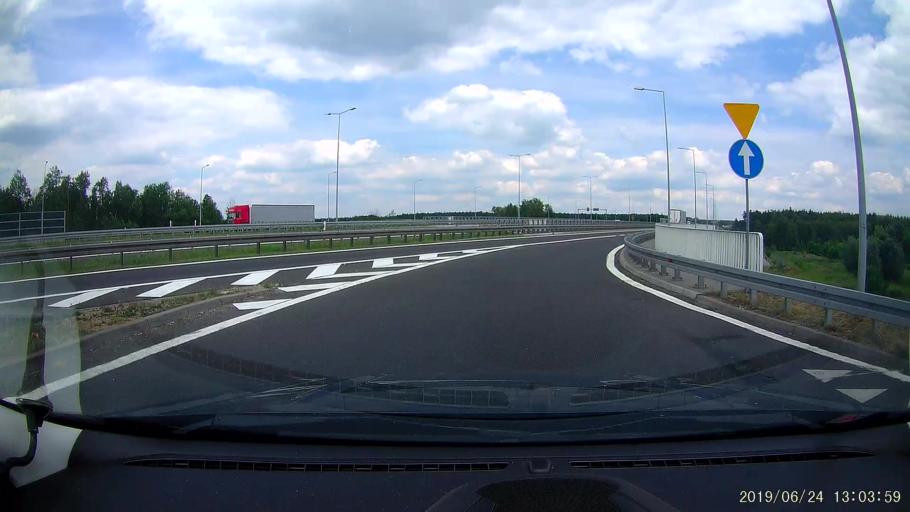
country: PL
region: Silesian Voivodeship
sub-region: Zory
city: Zory
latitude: 50.0769
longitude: 18.6640
